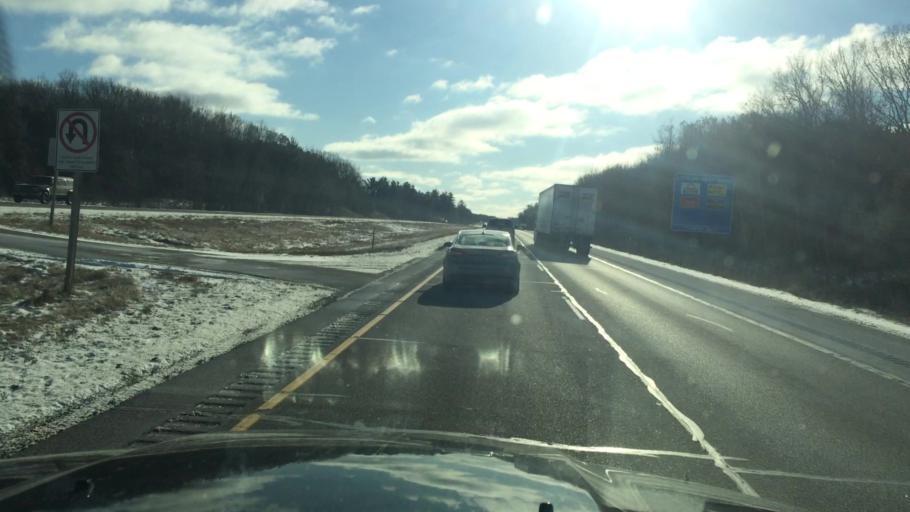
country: US
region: Wisconsin
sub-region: Portage County
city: Stevens Point
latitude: 44.5637
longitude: -89.5932
